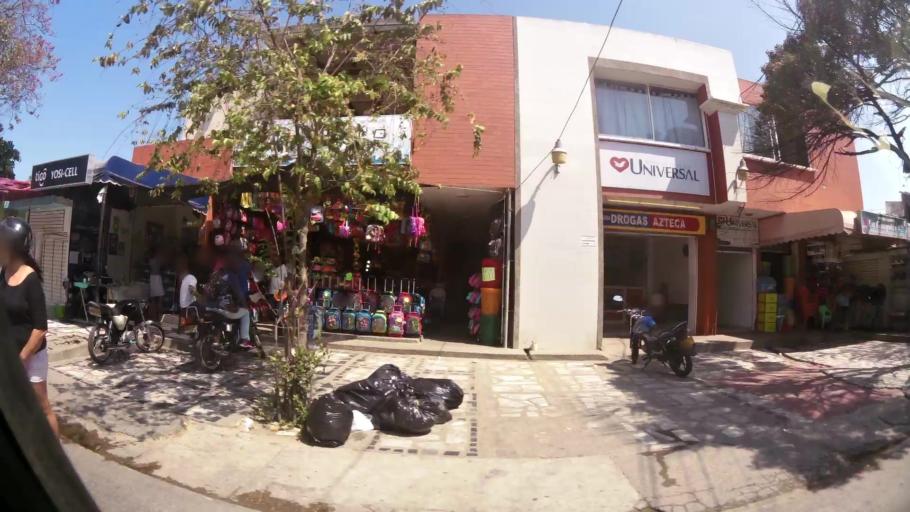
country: CO
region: Atlantico
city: Barranquilla
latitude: 10.9665
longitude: -74.8350
